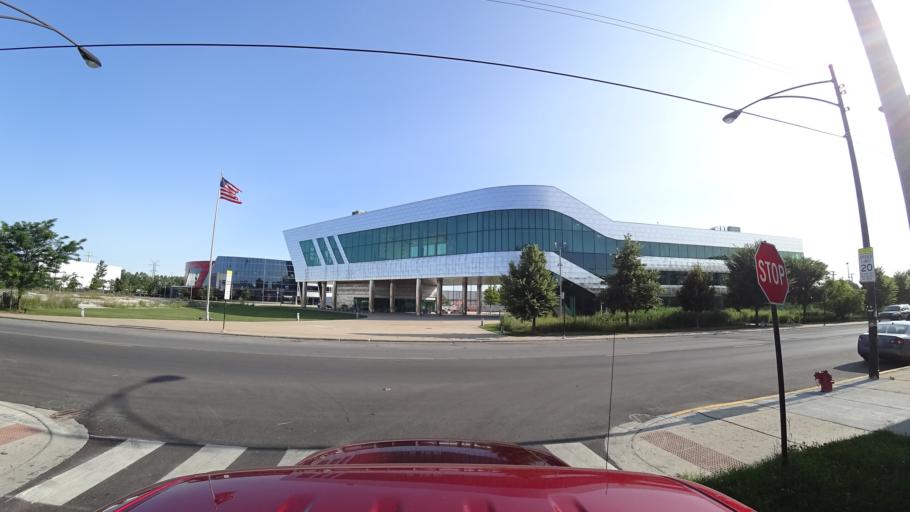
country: US
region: Illinois
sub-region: Cook County
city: Cicero
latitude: 41.8006
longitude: -87.7099
